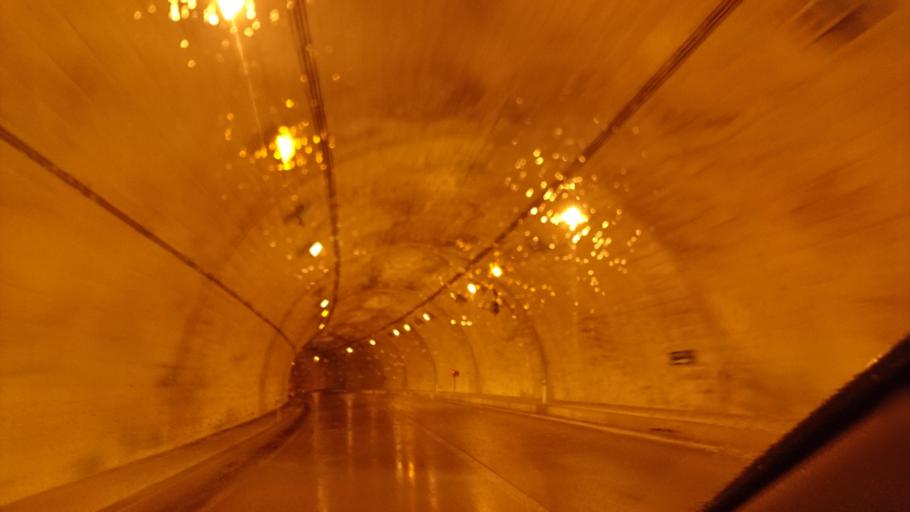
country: JP
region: Iwate
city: Mizusawa
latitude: 39.1248
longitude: 140.9143
